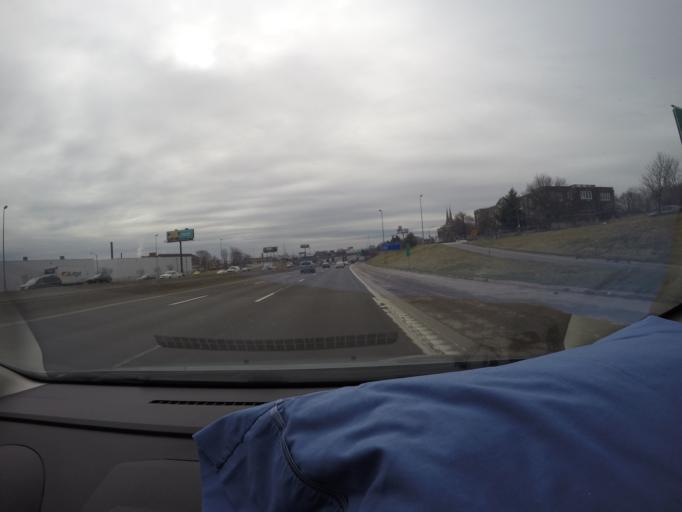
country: US
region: Illinois
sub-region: Madison County
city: Venice
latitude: 38.6646
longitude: -90.1989
